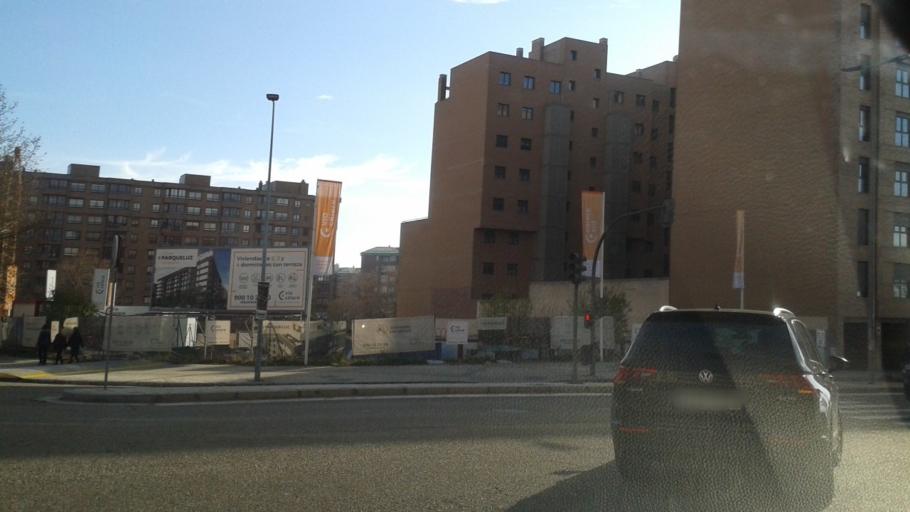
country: ES
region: Castille and Leon
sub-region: Provincia de Valladolid
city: Zaratan
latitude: 41.6359
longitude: -4.7615
